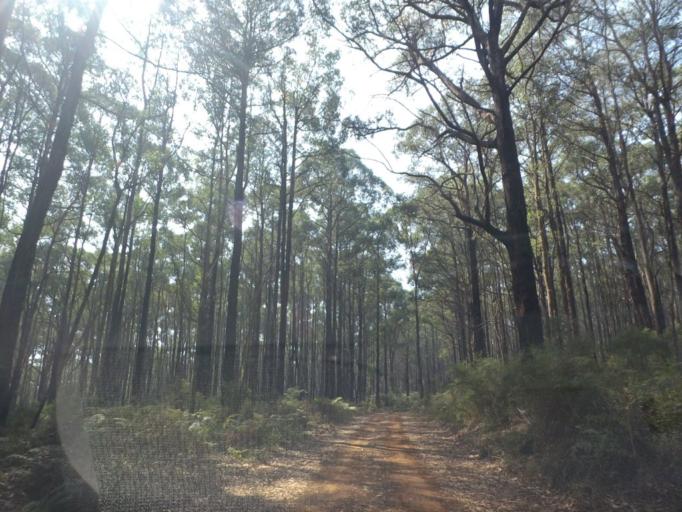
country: AU
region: Victoria
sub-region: Yarra Ranges
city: Millgrove
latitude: -37.5802
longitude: 145.6862
